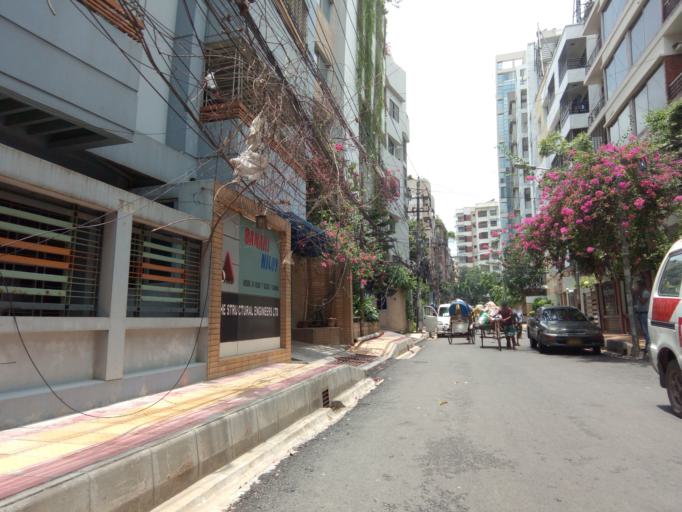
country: BD
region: Dhaka
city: Paltan
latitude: 23.7901
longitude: 90.4025
